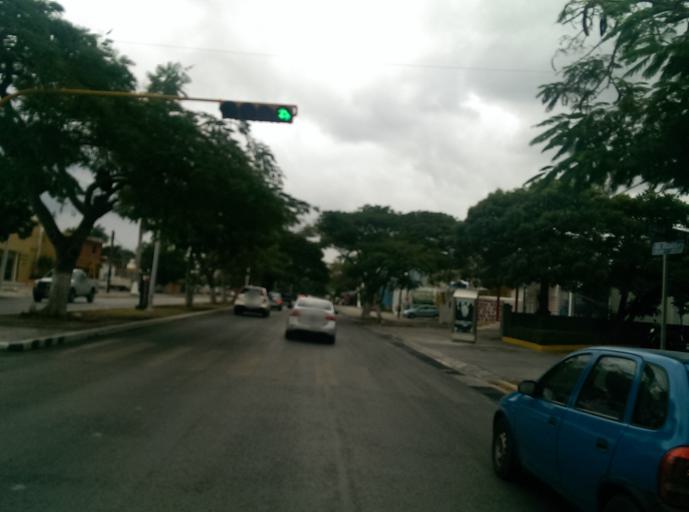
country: MX
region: Yucatan
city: Merida
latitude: 20.9824
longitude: -89.6396
